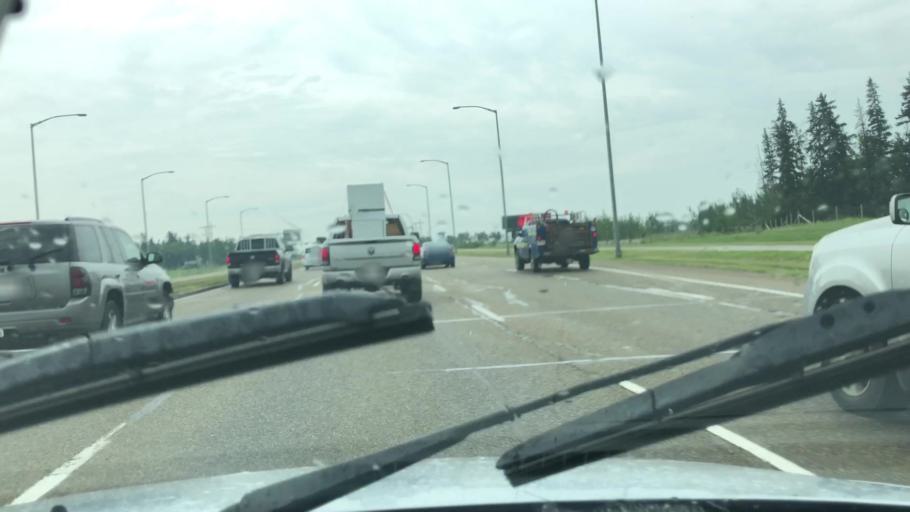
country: CA
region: Alberta
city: St. Albert
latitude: 53.6138
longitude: -113.5952
